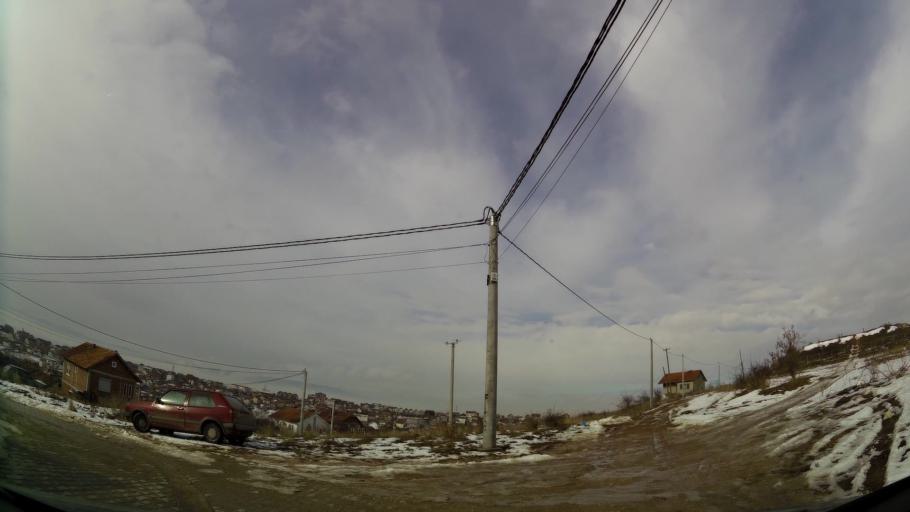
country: XK
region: Pristina
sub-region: Komuna e Prishtines
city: Pristina
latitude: 42.6855
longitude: 21.1692
